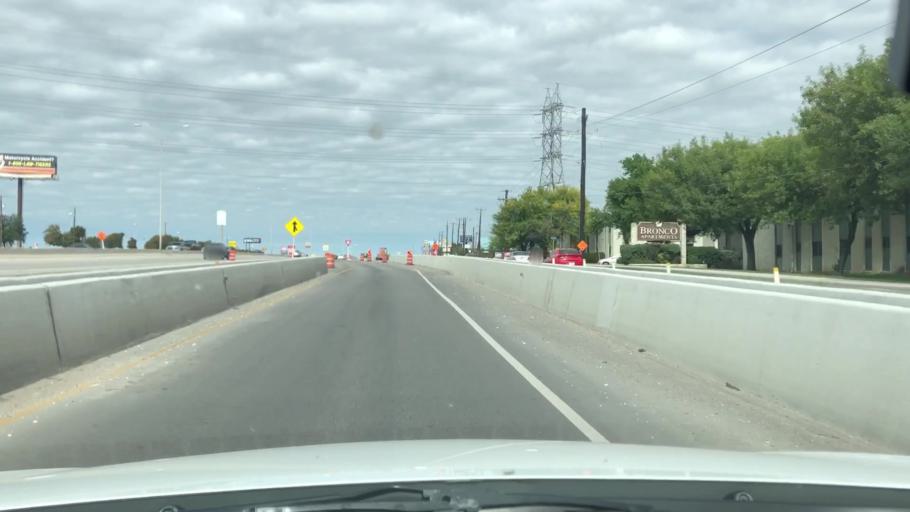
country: US
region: Texas
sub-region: Bexar County
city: Lackland Air Force Base
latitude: 29.4090
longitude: -98.6494
